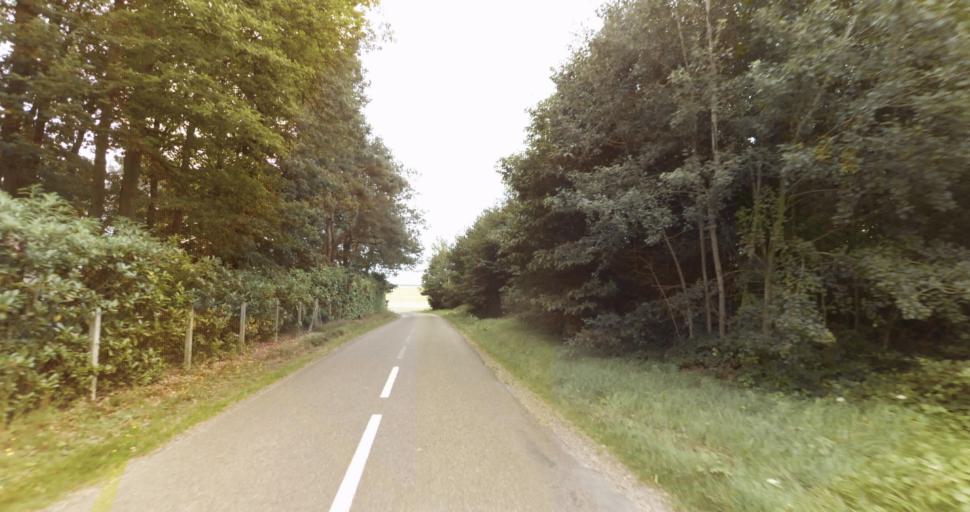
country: FR
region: Haute-Normandie
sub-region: Departement de l'Eure
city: Menilles
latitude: 48.9767
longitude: 1.2812
